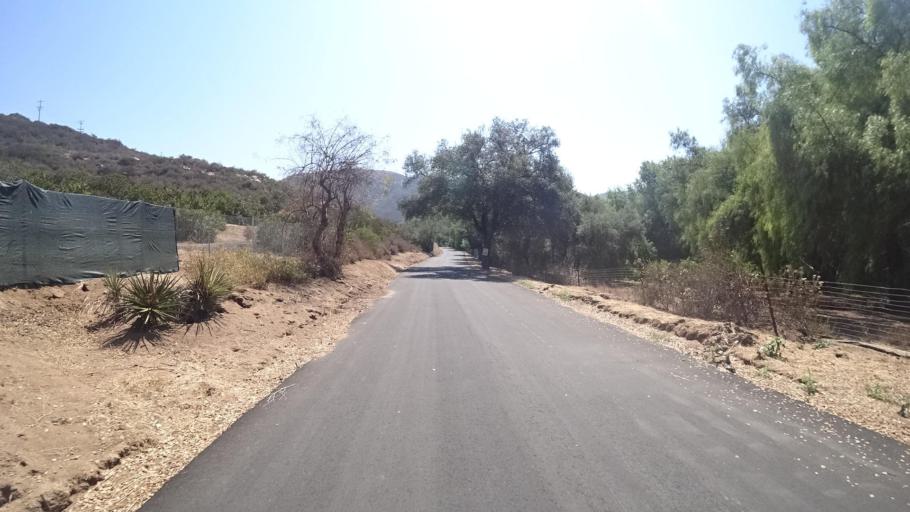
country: US
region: California
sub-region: San Diego County
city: Hidden Meadows
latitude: 33.2503
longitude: -117.1118
